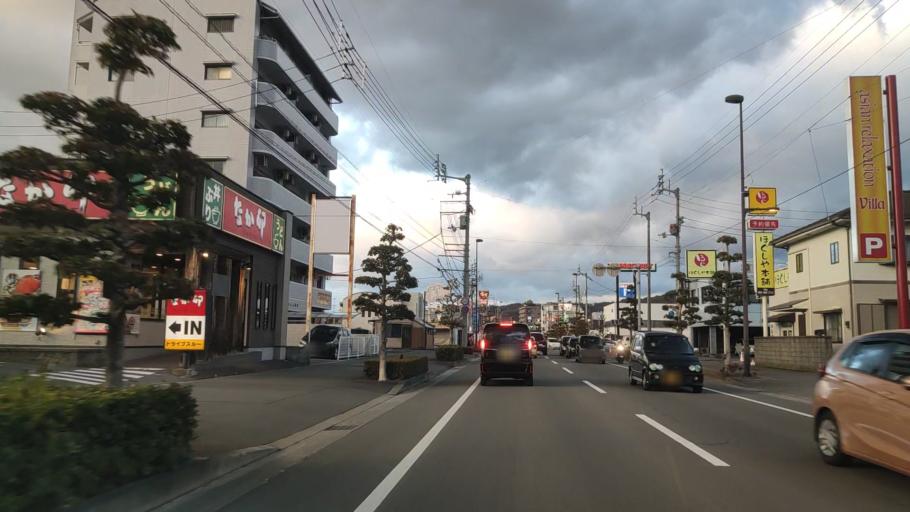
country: JP
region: Ehime
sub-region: Shikoku-chuo Shi
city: Matsuyama
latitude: 33.8343
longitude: 132.7871
